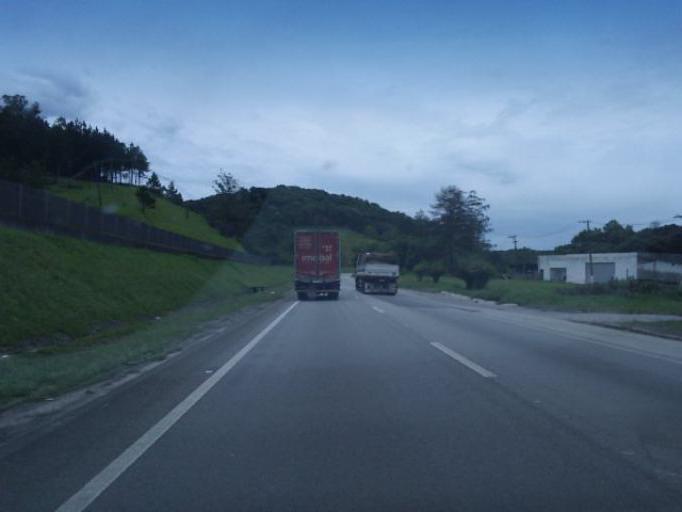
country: BR
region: Sao Paulo
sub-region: Juquitiba
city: Juquitiba
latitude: -23.9387
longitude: -47.0395
